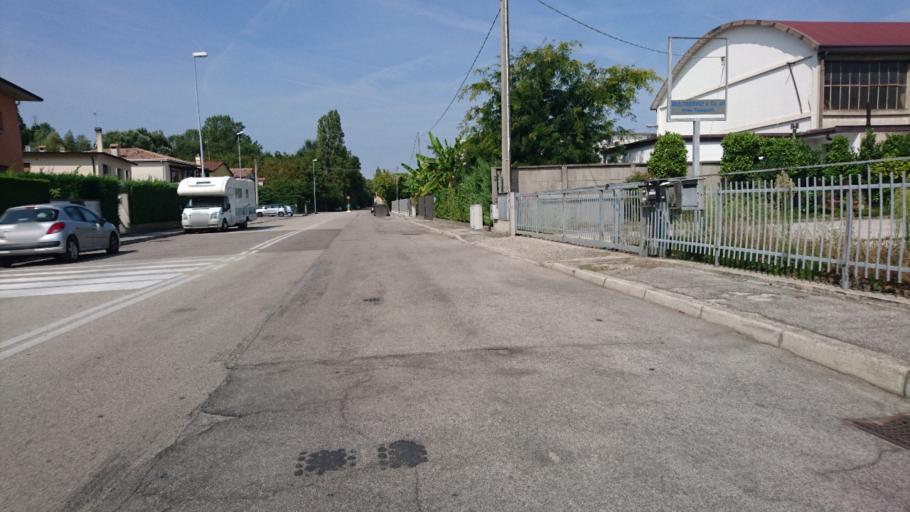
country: IT
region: Veneto
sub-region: Provincia di Padova
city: Mandriola-Sant'Agostino
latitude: 45.3682
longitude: 11.8497
